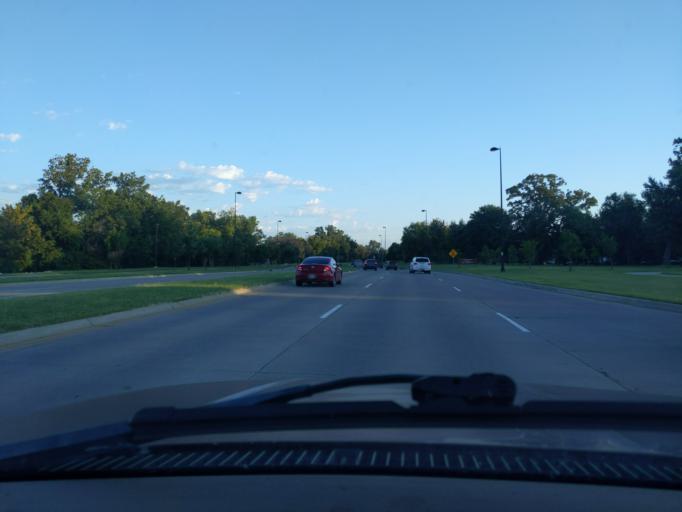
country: US
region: Oklahoma
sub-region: Tulsa County
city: Tulsa
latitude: 36.0909
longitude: -95.9844
